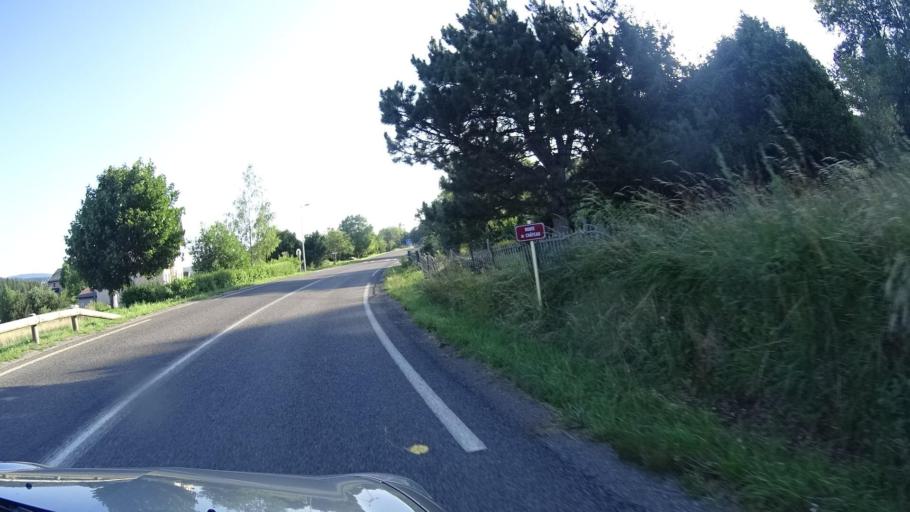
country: FR
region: Franche-Comte
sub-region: Departement du Jura
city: Longchaumois
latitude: 46.5077
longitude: 5.9556
